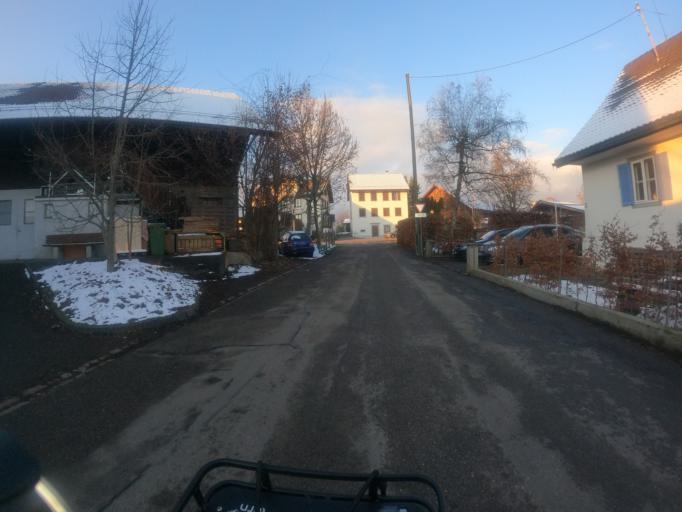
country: CH
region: Zurich
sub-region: Bezirk Affoltern
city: Affoltern / Unterdorf
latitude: 47.2889
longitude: 8.4422
